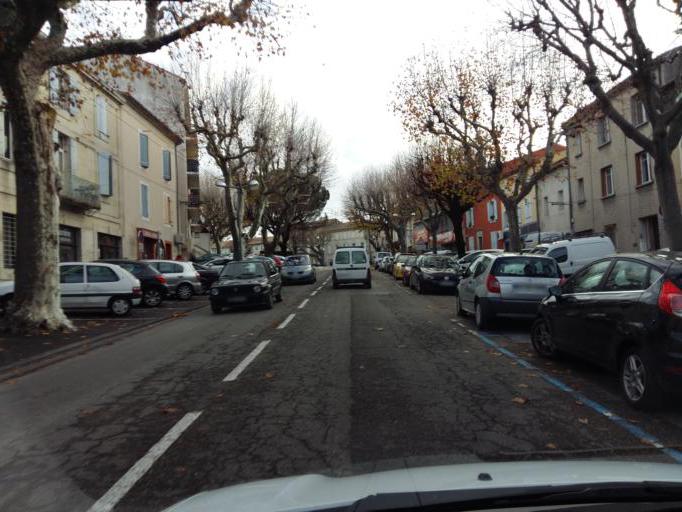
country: FR
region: Provence-Alpes-Cote d'Azur
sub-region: Departement du Vaucluse
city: Valreas
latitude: 44.3840
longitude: 4.9877
